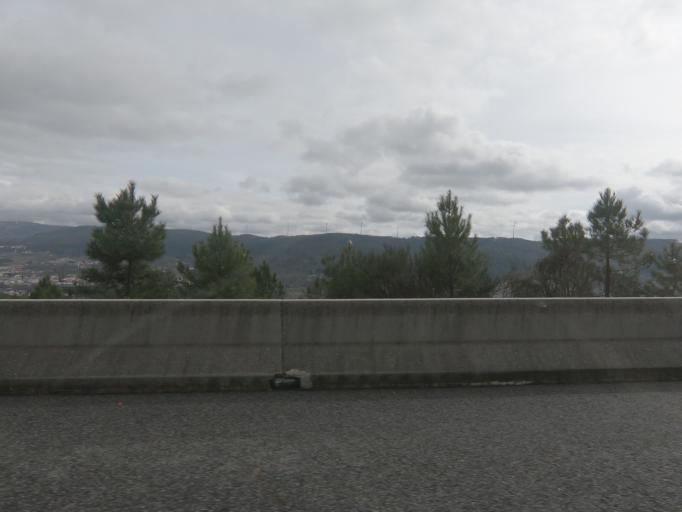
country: PT
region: Vila Real
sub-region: Vila Pouca de Aguiar
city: Vila Pouca de Aguiar
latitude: 41.5368
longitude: -7.6315
